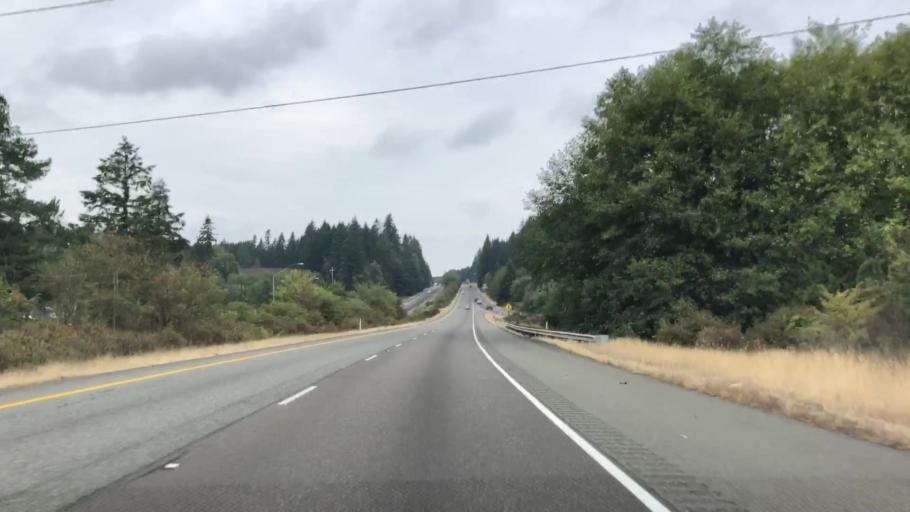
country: US
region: Washington
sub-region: Kitsap County
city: Bethel
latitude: 47.5022
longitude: -122.6464
